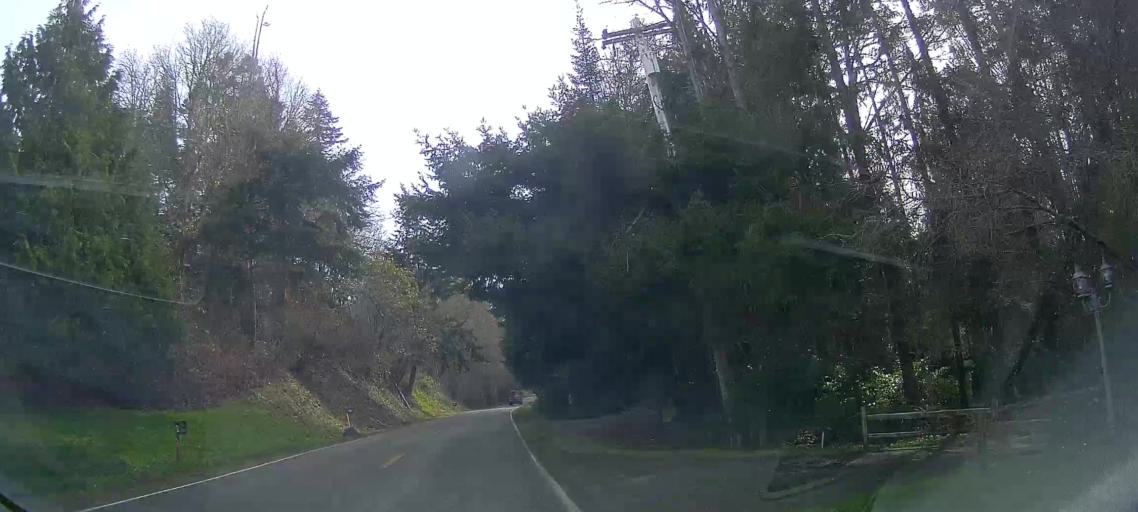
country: US
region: Washington
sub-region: Island County
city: Langley
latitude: 48.0785
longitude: -122.3912
